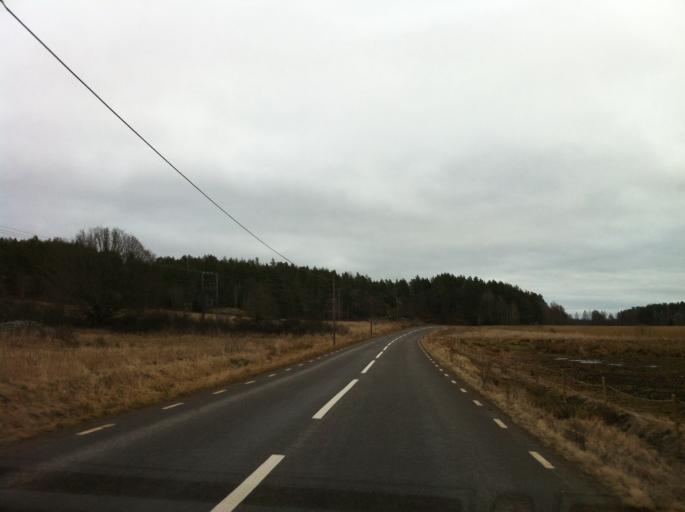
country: SE
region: Kalmar
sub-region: Vasterviks Kommun
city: Overum
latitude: 57.9101
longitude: 16.1777
